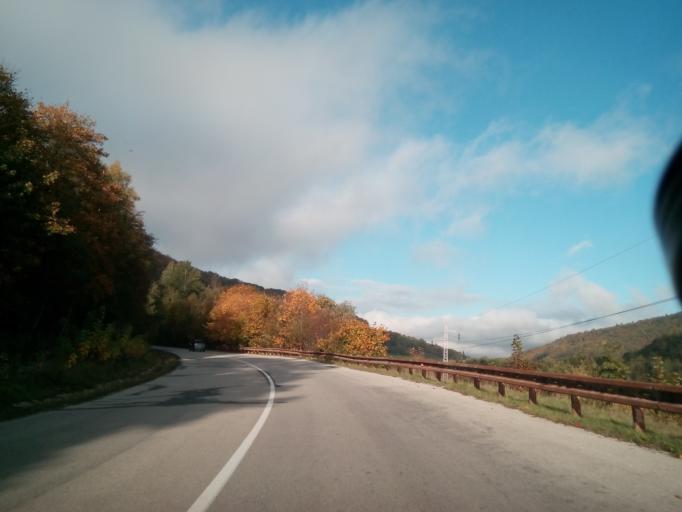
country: SK
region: Kosicky
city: Gelnica
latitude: 48.8960
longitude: 20.9964
